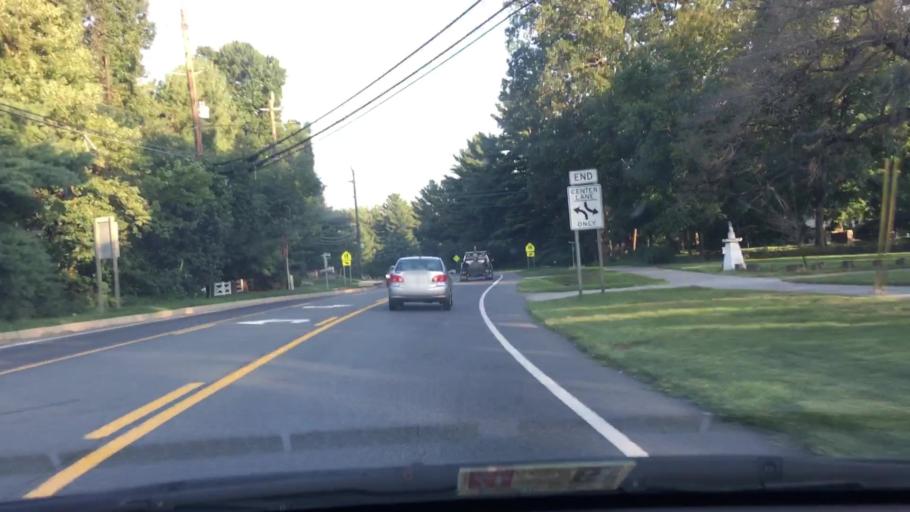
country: US
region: Maryland
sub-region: Montgomery County
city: Redland
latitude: 39.1419
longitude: -77.1384
